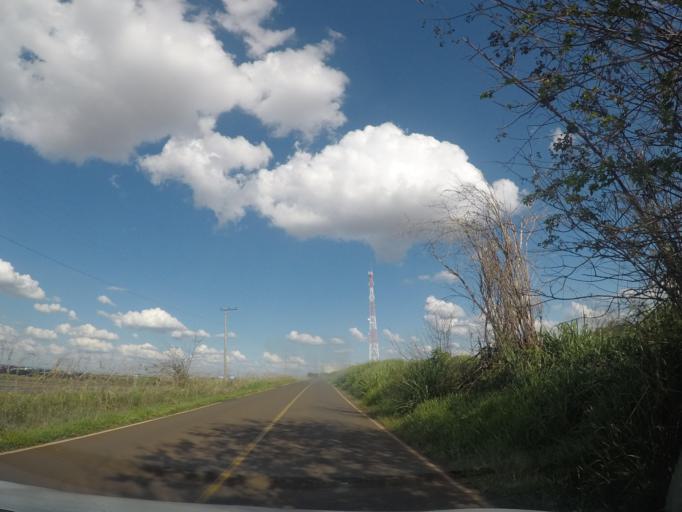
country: BR
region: Sao Paulo
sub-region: Sumare
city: Sumare
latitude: -22.8555
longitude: -47.3135
